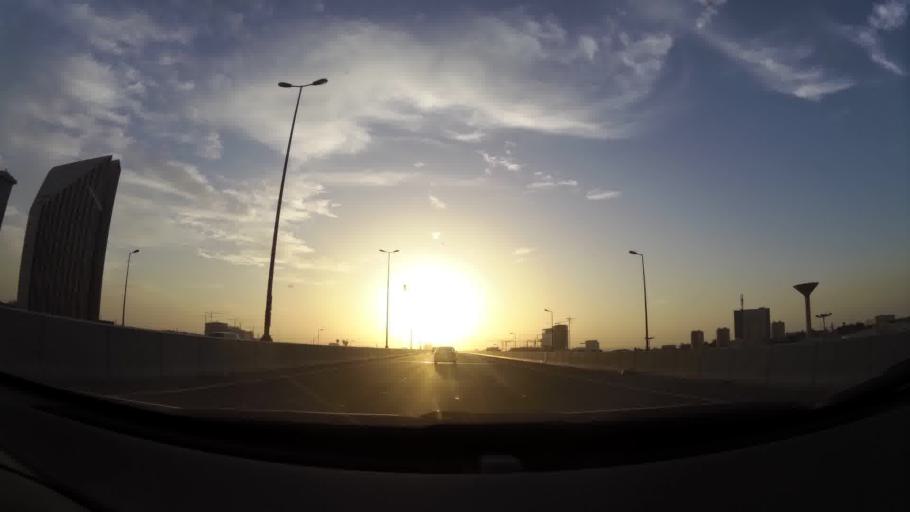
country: KW
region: Al Asimah
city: Ar Rabiyah
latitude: 29.3358
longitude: 47.9164
